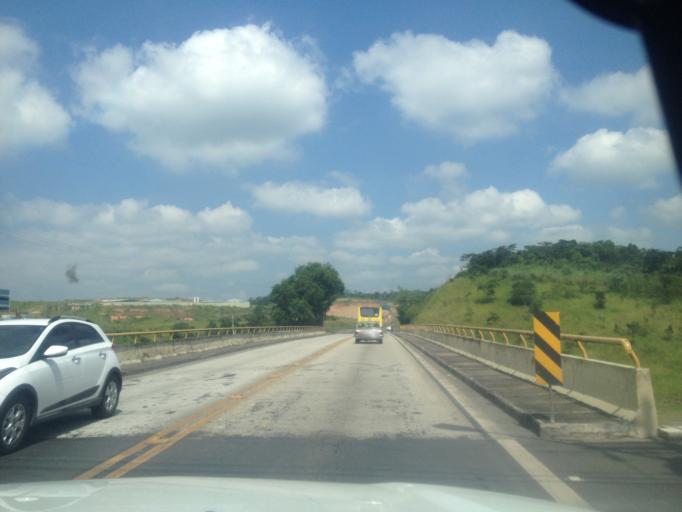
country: BR
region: Rio de Janeiro
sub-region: Volta Redonda
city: Volta Redonda
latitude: -22.5893
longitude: -44.0814
